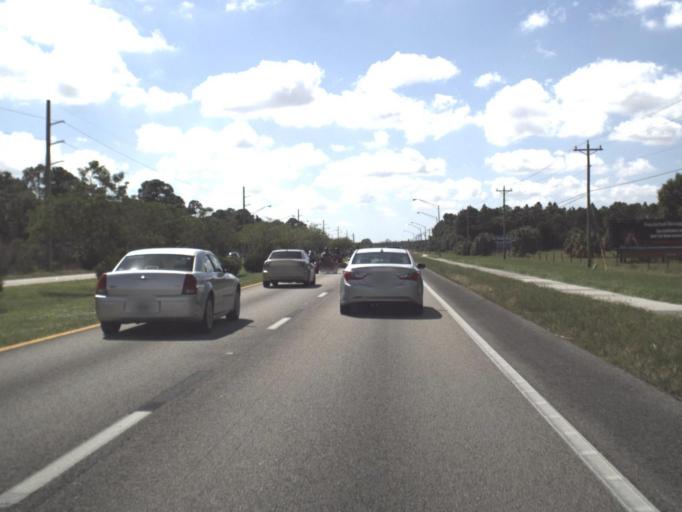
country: US
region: Florida
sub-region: Lee County
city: Palmona Park
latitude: 26.6934
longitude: -81.9011
